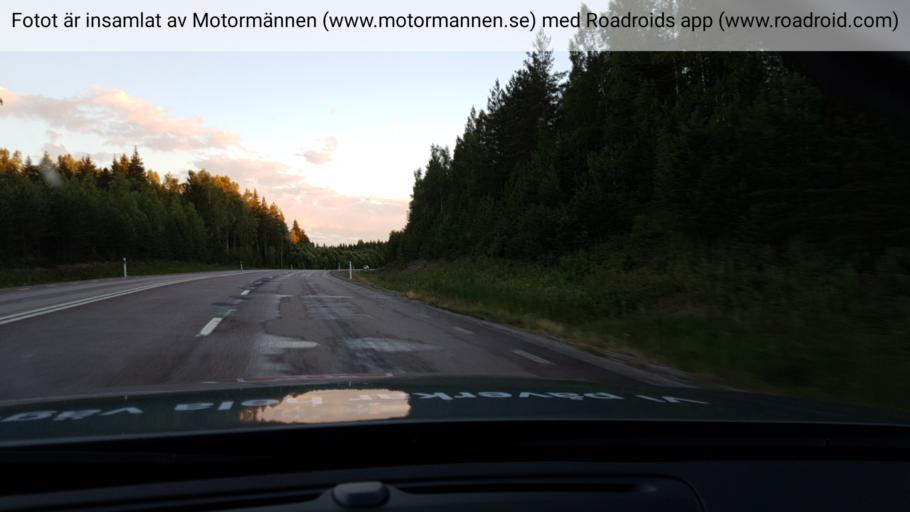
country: SE
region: Vaestmanland
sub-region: Fagersta Kommun
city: Fagersta
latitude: 59.9499
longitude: 15.7512
